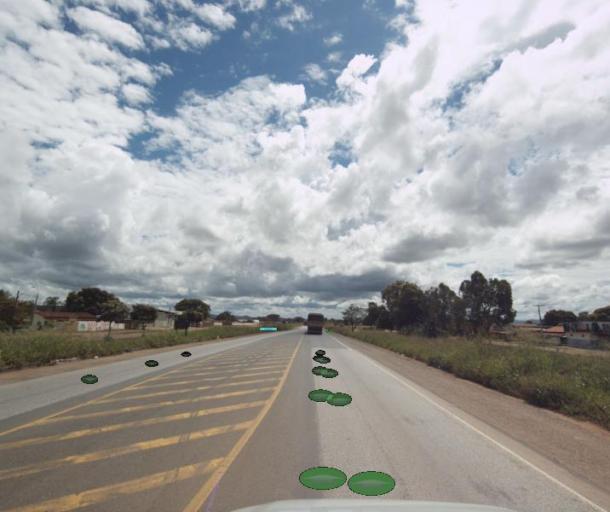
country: BR
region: Goias
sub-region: Uruacu
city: Uruacu
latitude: -14.3135
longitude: -49.1497
